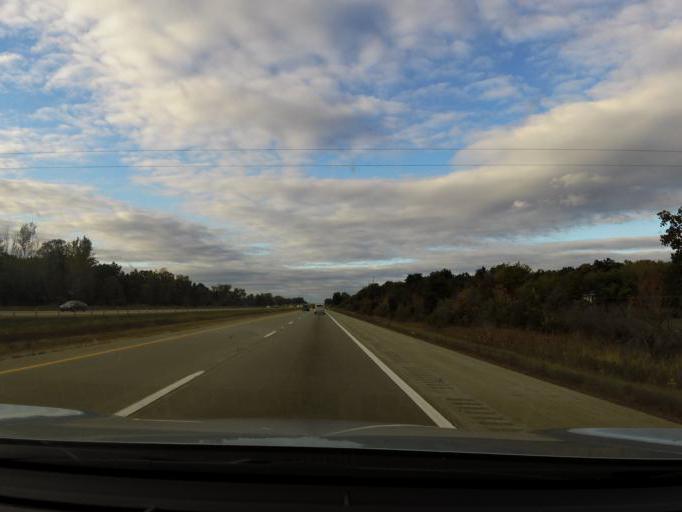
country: US
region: Michigan
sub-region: Genesee County
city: Linden
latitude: 42.7254
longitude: -83.7630
